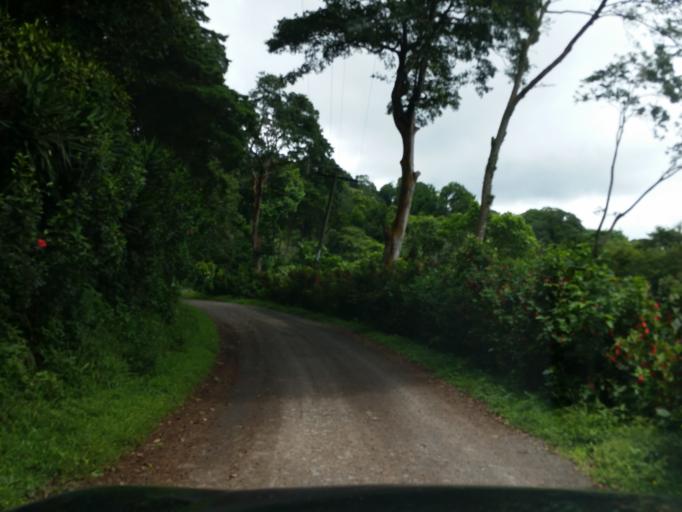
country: NI
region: Matagalpa
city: Matagalpa
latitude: 12.9981
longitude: -85.9139
